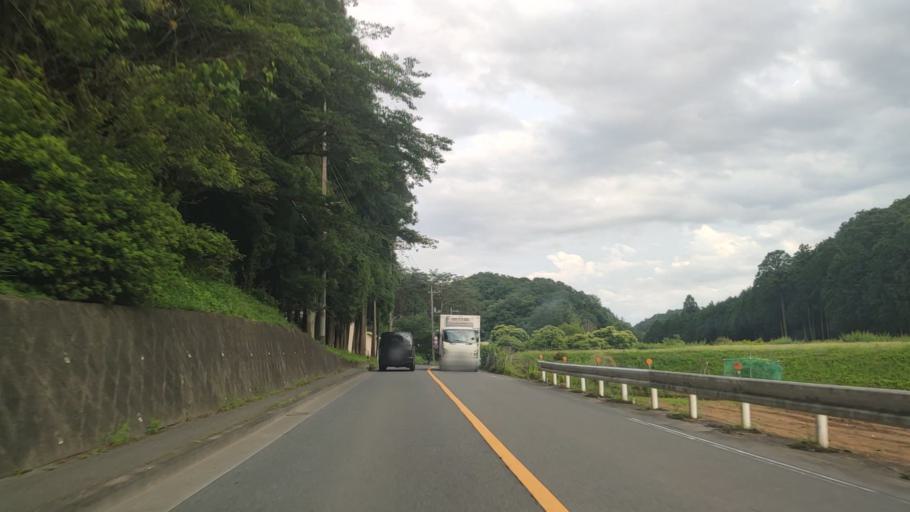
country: JP
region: Saitama
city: Hanno
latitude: 35.8178
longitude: 139.2959
